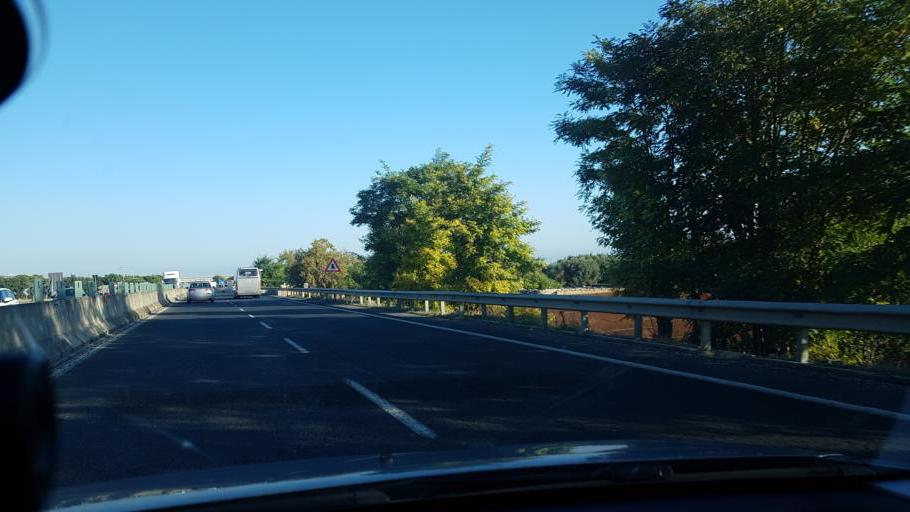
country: IT
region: Apulia
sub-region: Provincia di Bari
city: Monopoli
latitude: 40.9020
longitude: 17.3269
